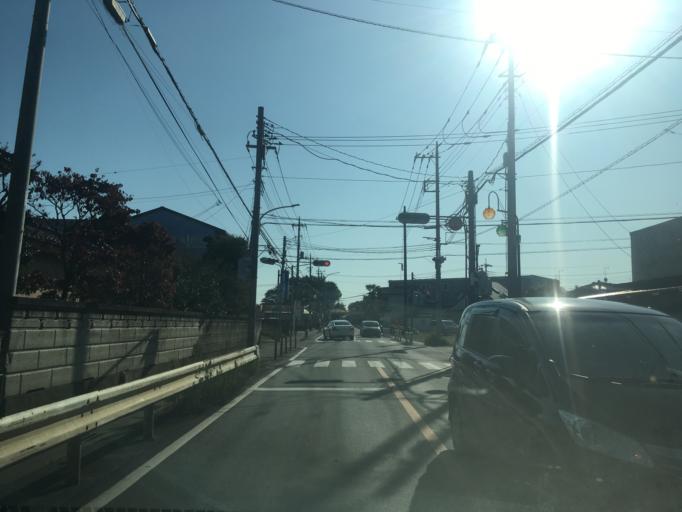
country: JP
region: Saitama
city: Kawagoe
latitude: 35.8757
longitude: 139.4742
